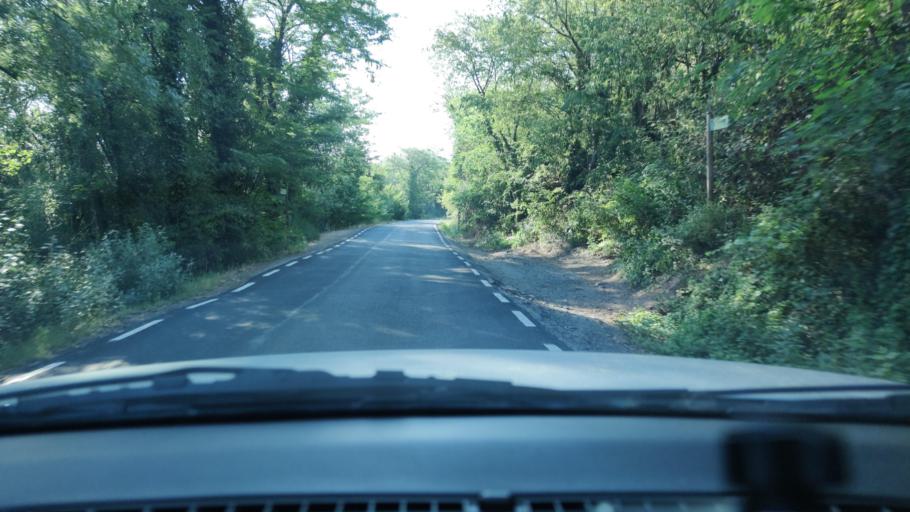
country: ES
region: Catalonia
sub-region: Provincia de Lleida
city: Camarasa
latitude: 41.8695
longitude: 0.8627
